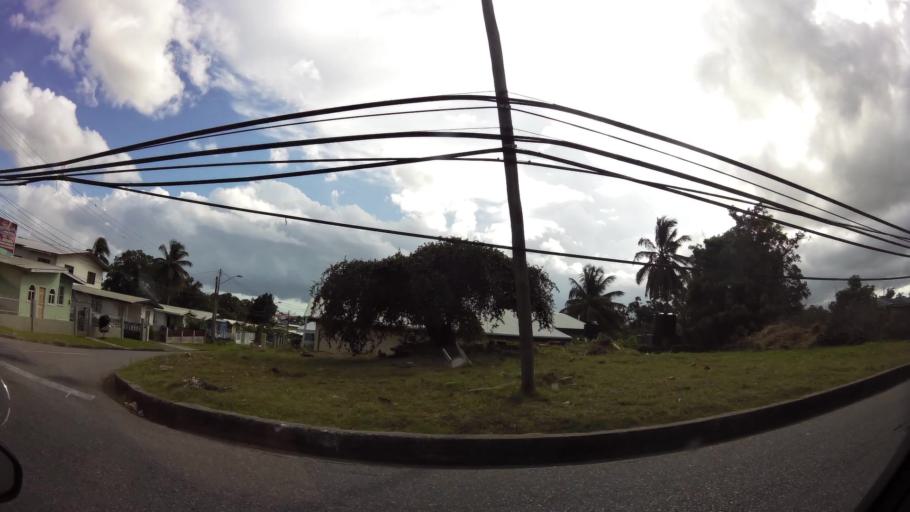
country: TT
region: City of San Fernando
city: Mon Repos
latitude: 10.2674
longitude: -61.4538
